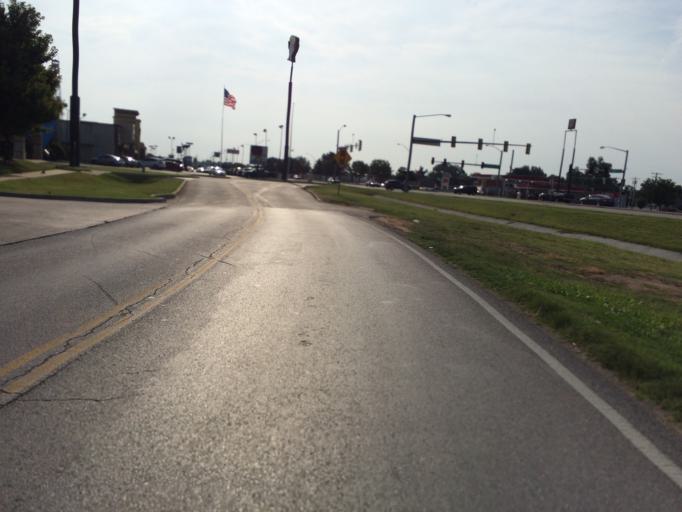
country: US
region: Oklahoma
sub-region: Cleveland County
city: Norman
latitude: 35.2189
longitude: -97.4825
